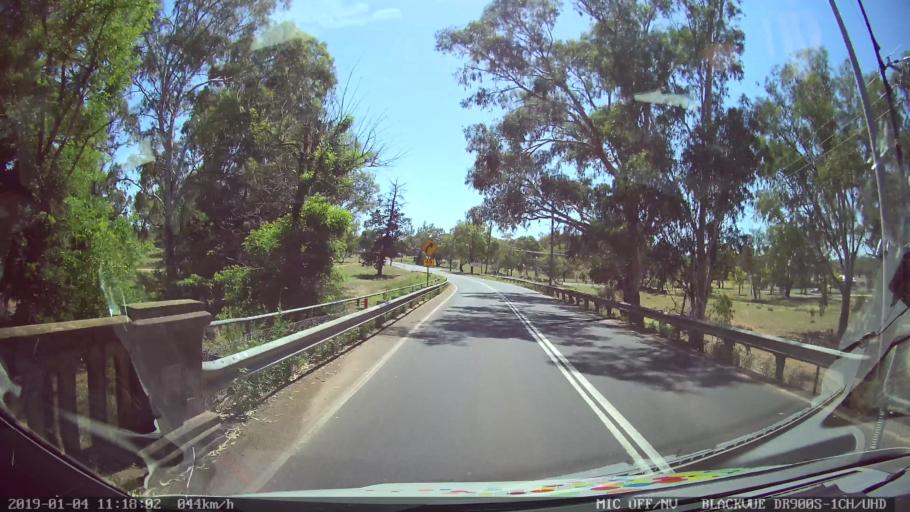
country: AU
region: New South Wales
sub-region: Cabonne
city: Molong
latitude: -33.1859
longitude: 148.6996
